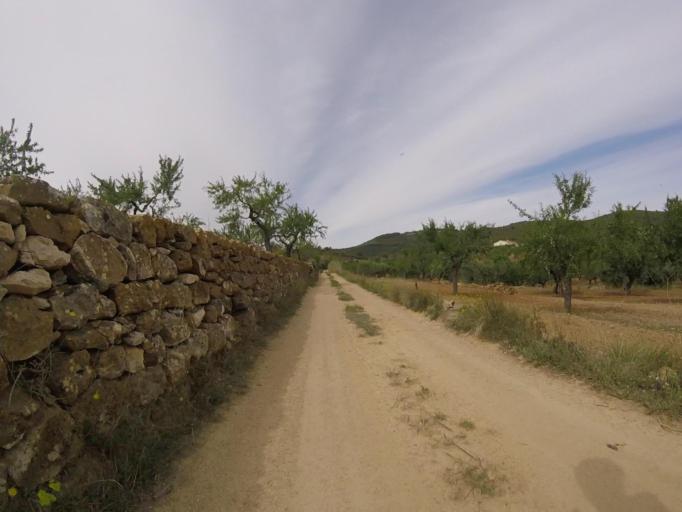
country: ES
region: Valencia
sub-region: Provincia de Castello
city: Cabanes
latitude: 40.1909
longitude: 0.0971
